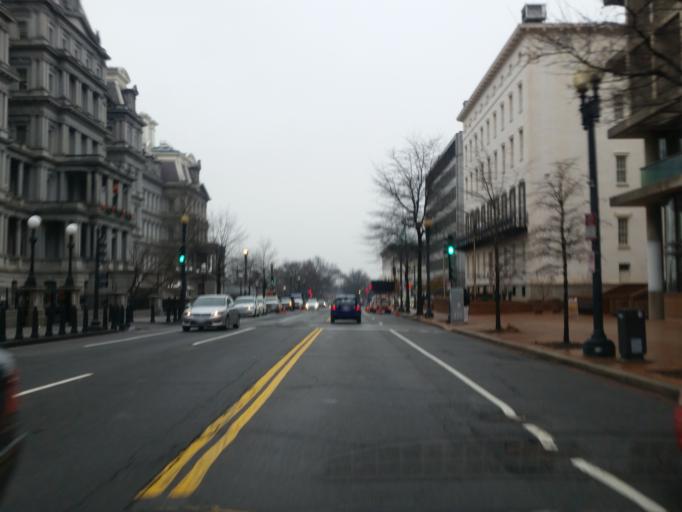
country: US
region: Washington, D.C.
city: Washington, D.C.
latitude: 38.8982
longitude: -77.0394
